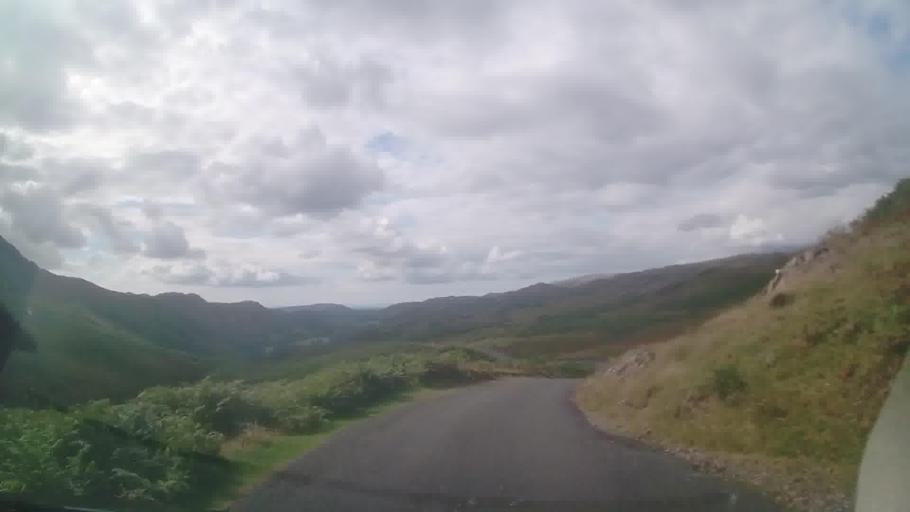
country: GB
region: England
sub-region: Cumbria
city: Millom
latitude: 54.4026
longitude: -3.1978
